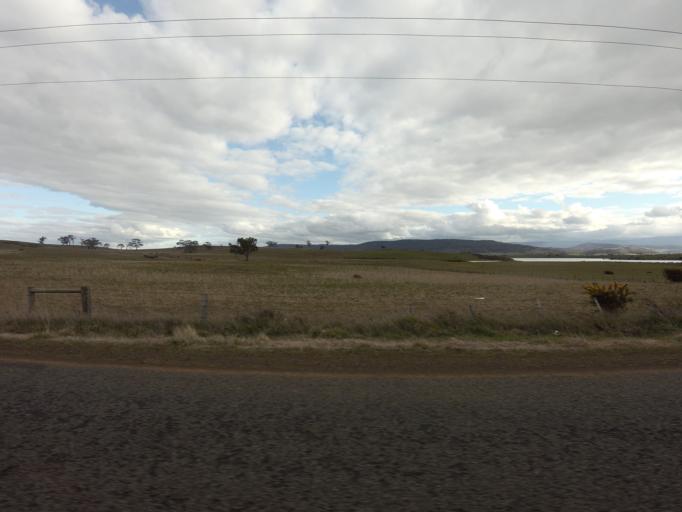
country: AU
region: Tasmania
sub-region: Northern Midlands
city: Evandale
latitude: -41.9046
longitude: 147.4526
